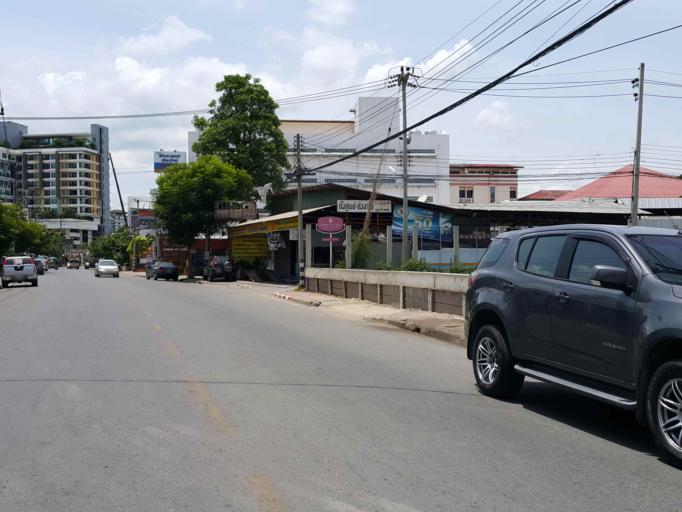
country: TH
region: Chiang Mai
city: Chiang Mai
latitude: 18.7695
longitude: 99.0005
